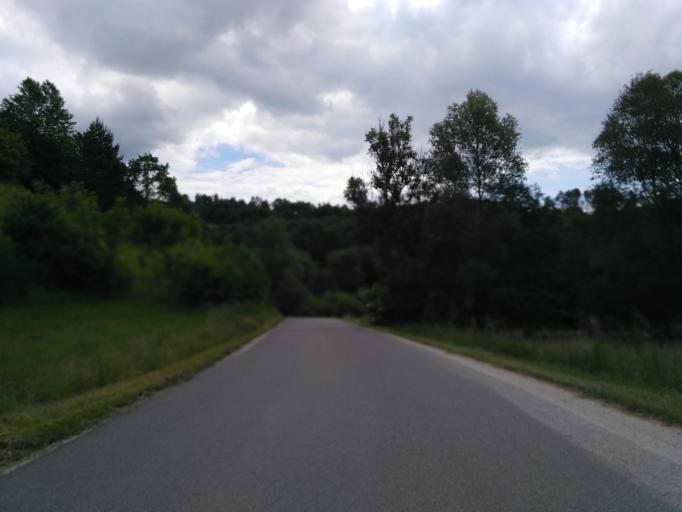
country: PL
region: Subcarpathian Voivodeship
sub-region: Powiat przeworski
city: Jawornik Polski
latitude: 49.8487
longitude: 22.3036
